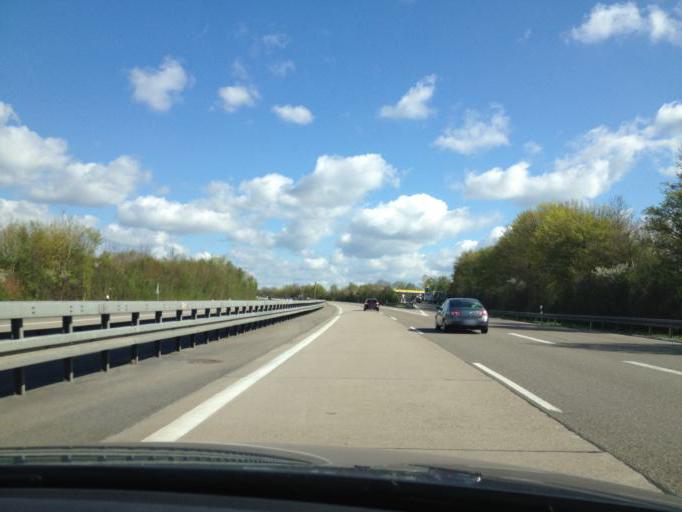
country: DE
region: Baden-Wuerttemberg
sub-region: Regierungsbezirk Stuttgart
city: Widdern
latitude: 49.3207
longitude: 9.4130
